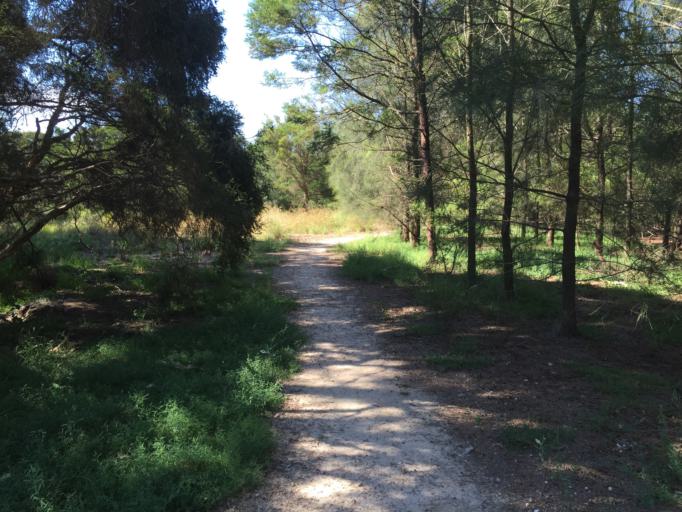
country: AU
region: New South Wales
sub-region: Blacktown
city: Stanhope Gardens
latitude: -33.7215
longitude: 150.9098
